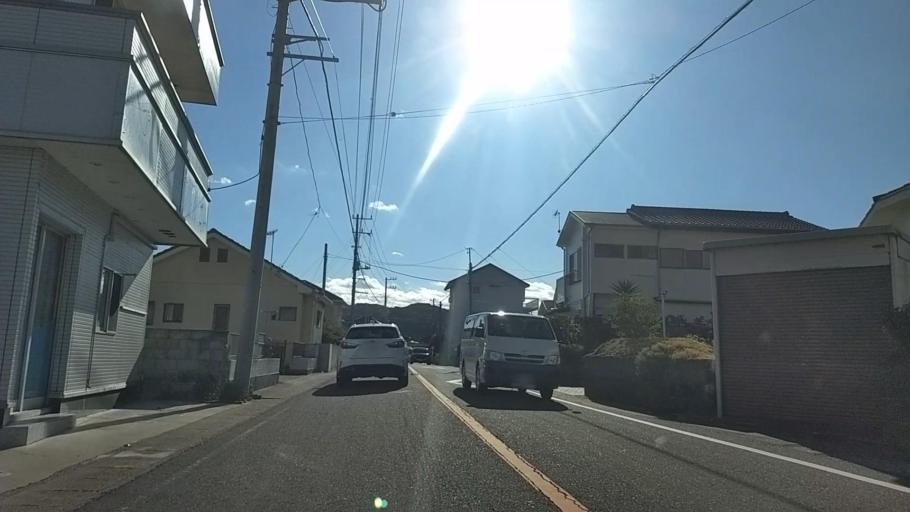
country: JP
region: Chiba
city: Tateyama
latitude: 35.1421
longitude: 139.8356
